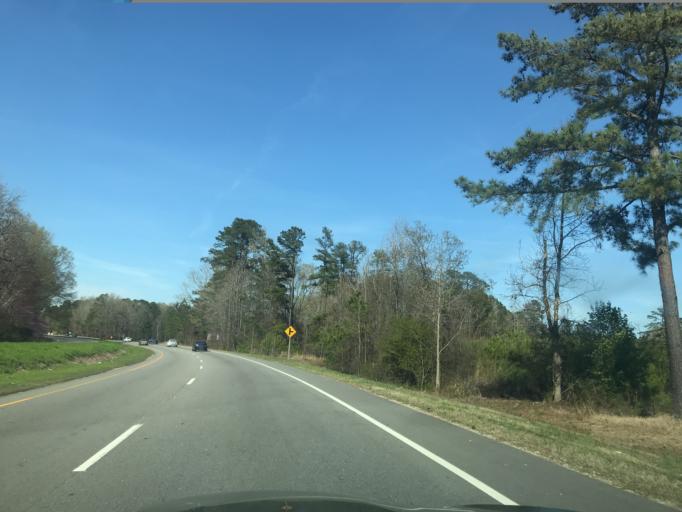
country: US
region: North Carolina
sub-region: Wake County
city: Garner
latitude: 35.6771
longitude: -78.6875
